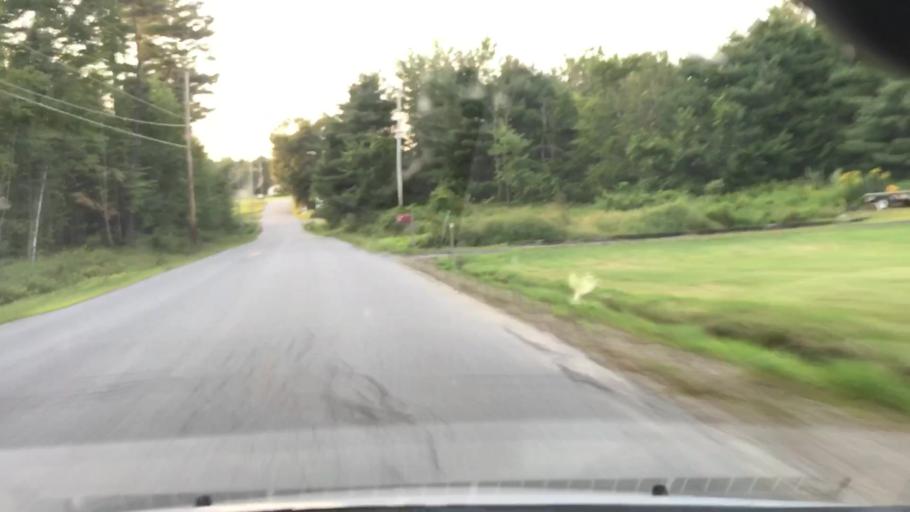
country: US
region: New Hampshire
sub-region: Grafton County
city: North Haverhill
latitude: 44.0743
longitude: -72.0154
